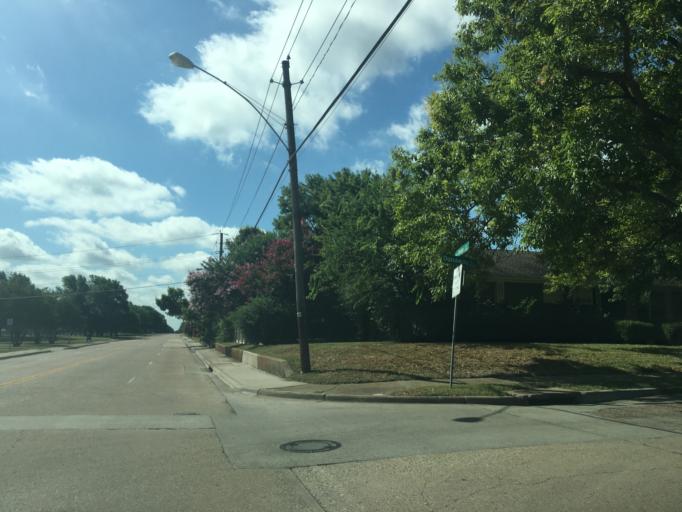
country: US
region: Texas
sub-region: Dallas County
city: Garland
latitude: 32.8453
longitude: -96.6572
